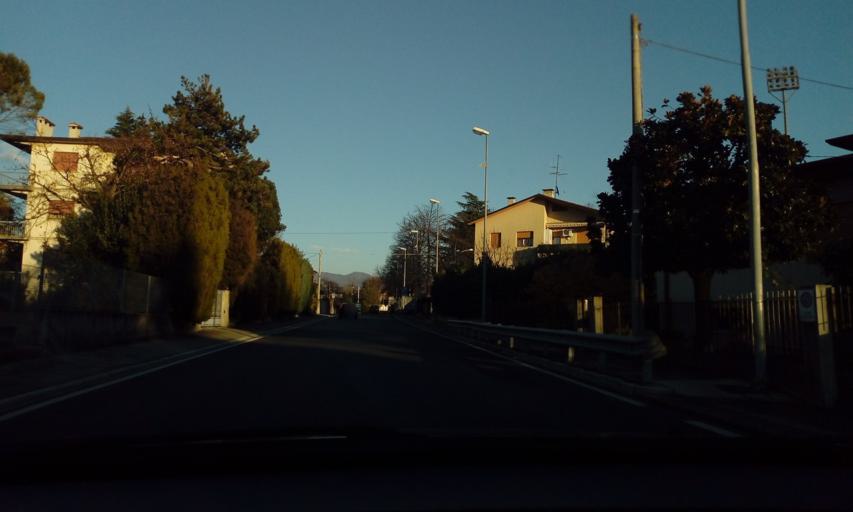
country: IT
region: Friuli Venezia Giulia
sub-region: Provincia di Gorizia
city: Gorizia
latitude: 45.9332
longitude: 13.6021
